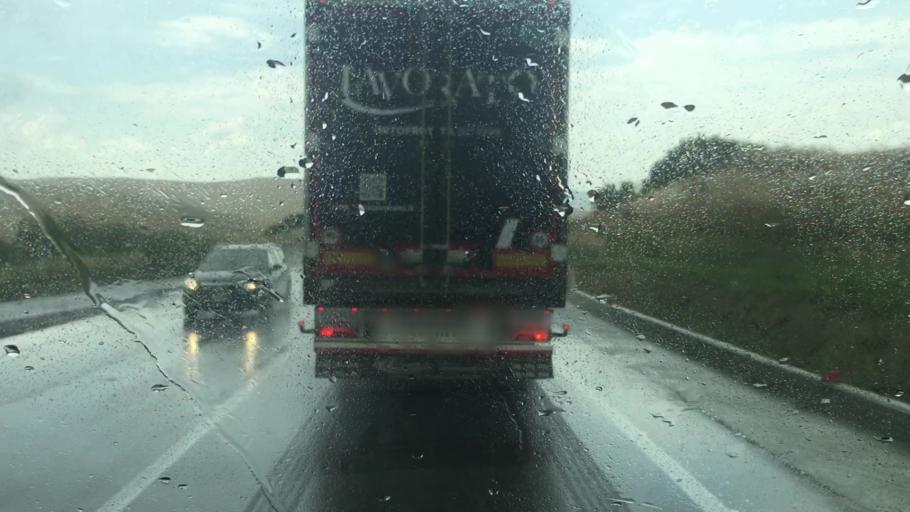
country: IT
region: Basilicate
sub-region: Provincia di Matera
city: Matera
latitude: 40.6312
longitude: 16.5923
